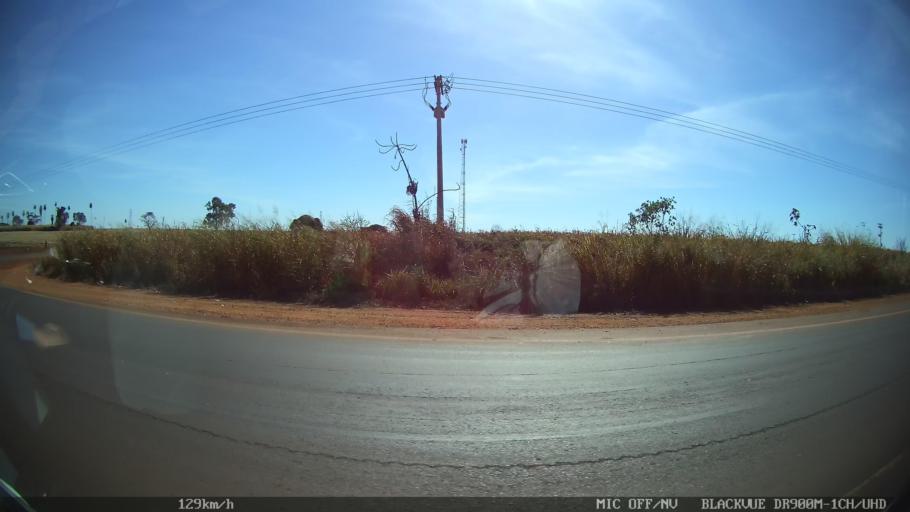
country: BR
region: Sao Paulo
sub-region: Barretos
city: Barretos
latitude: -20.4648
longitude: -48.4747
